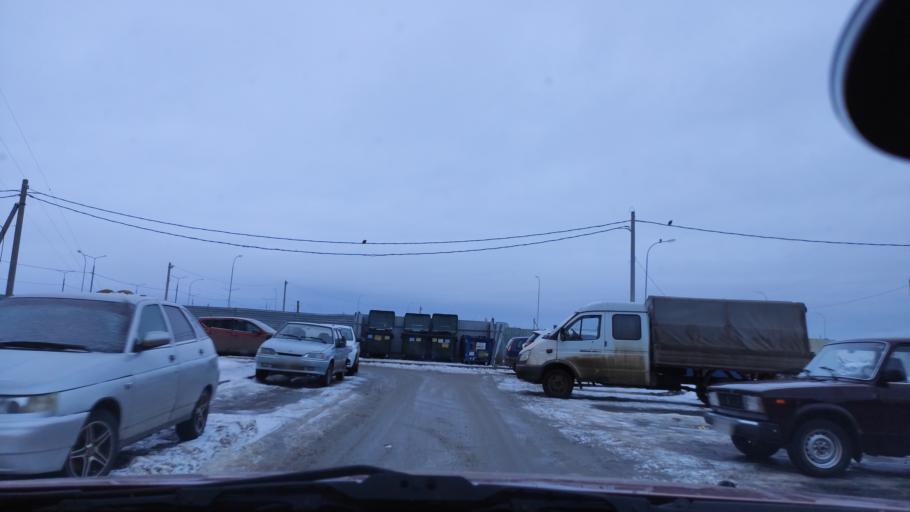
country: RU
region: Tambov
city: Tambov
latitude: 52.7770
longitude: 41.4134
